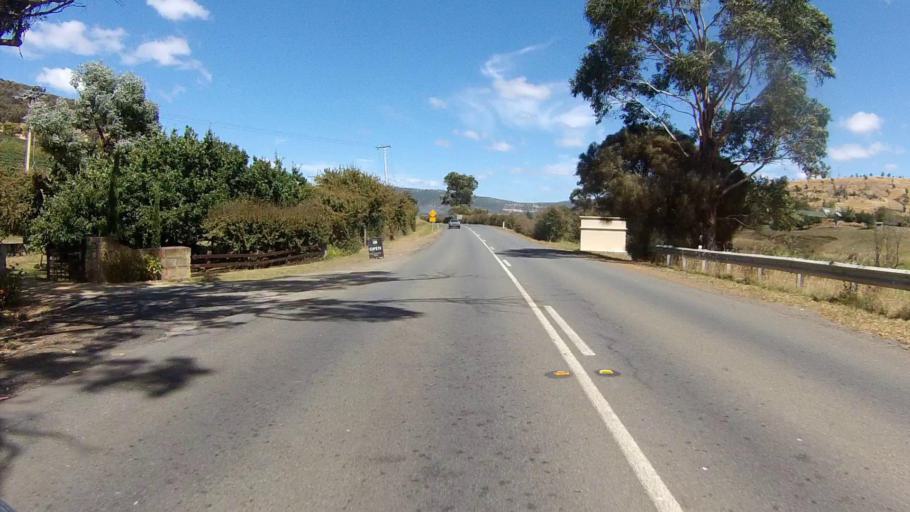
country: AU
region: Tasmania
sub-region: Clarence
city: Cambridge
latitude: -42.7391
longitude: 147.4273
